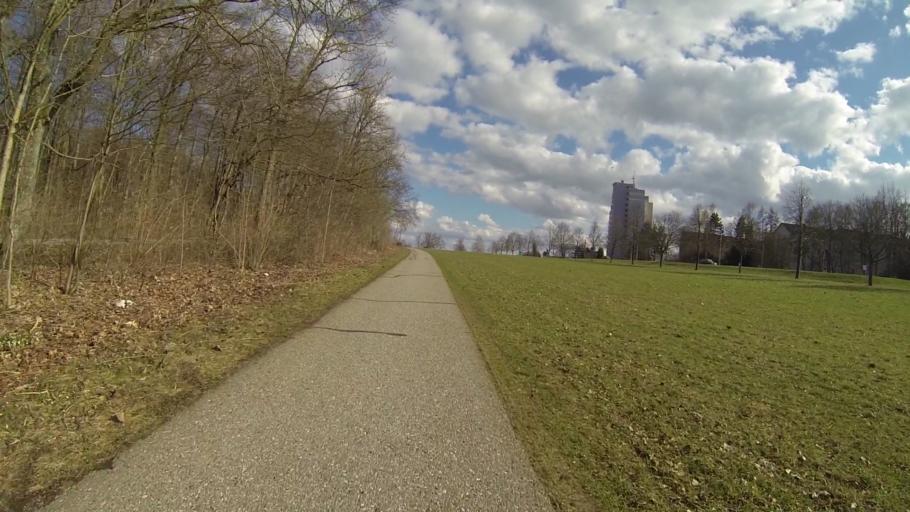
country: DE
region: Baden-Wuerttemberg
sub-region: Regierungsbezirk Stuttgart
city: Heidenheim an der Brenz
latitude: 48.6932
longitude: 10.1380
